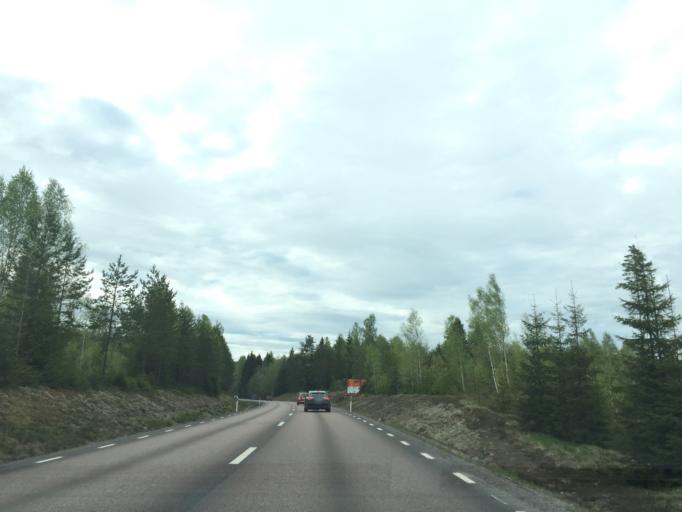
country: SE
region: Vaermland
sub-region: Eda Kommun
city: Charlottenberg
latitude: 59.9141
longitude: 12.2747
